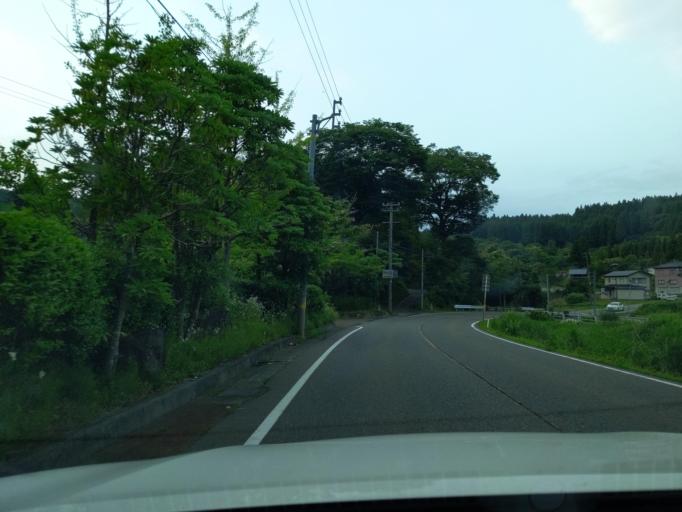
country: JP
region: Niigata
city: Nagaoka
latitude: 37.4397
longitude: 138.7103
